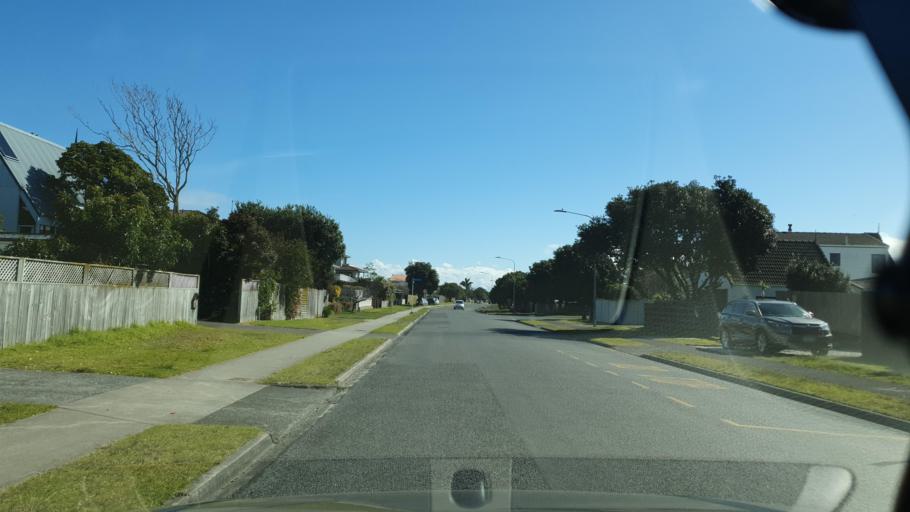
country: NZ
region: Bay of Plenty
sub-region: Tauranga City
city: Tauranga
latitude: -37.7009
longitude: 176.2905
